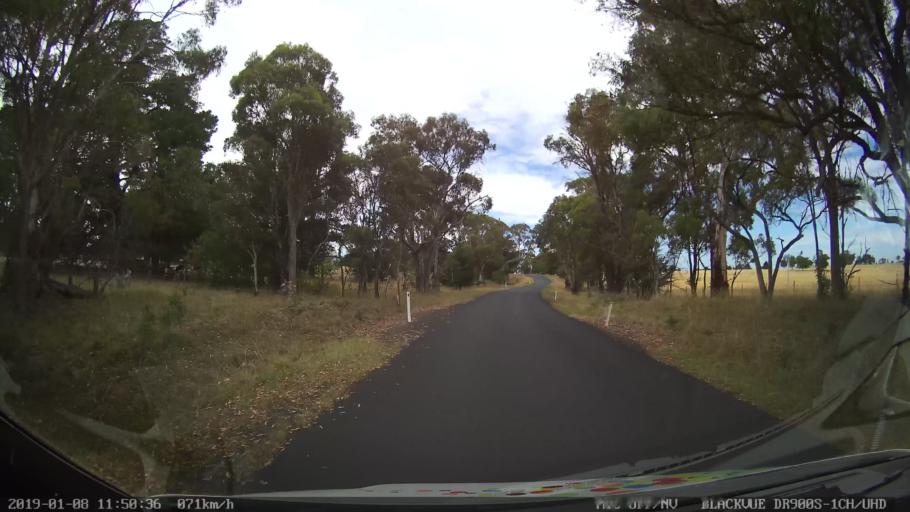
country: AU
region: New South Wales
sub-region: Armidale Dumaresq
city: Armidale
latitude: -30.3844
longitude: 151.5576
